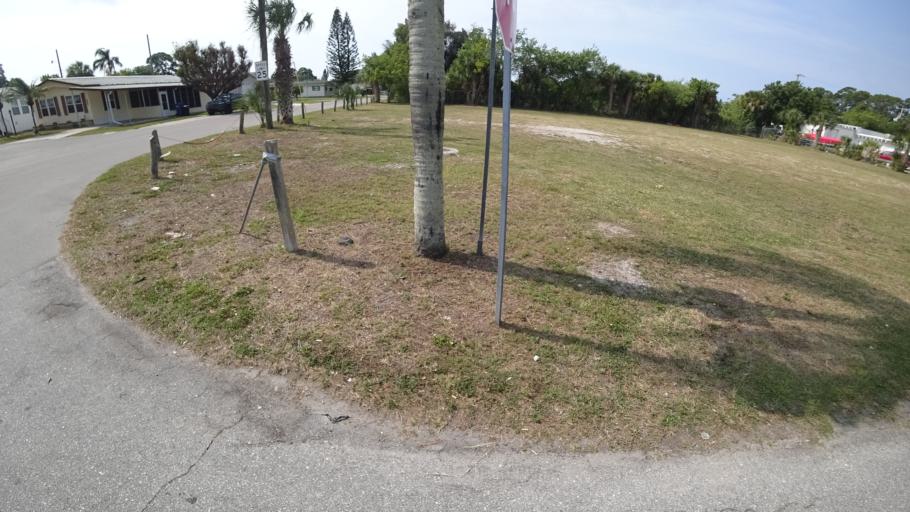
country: US
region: Florida
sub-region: Manatee County
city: South Bradenton
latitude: 27.4528
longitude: -82.5739
